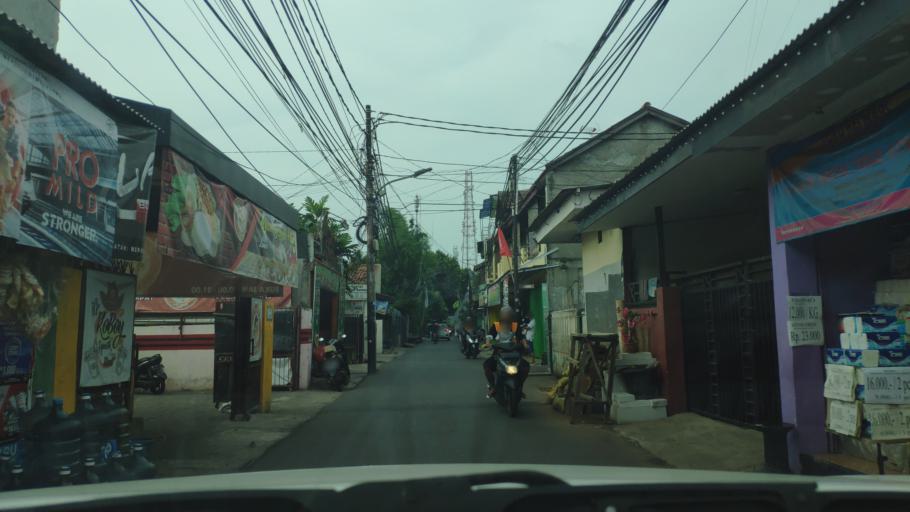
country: ID
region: Jakarta Raya
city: Jakarta
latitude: -6.1865
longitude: 106.8014
